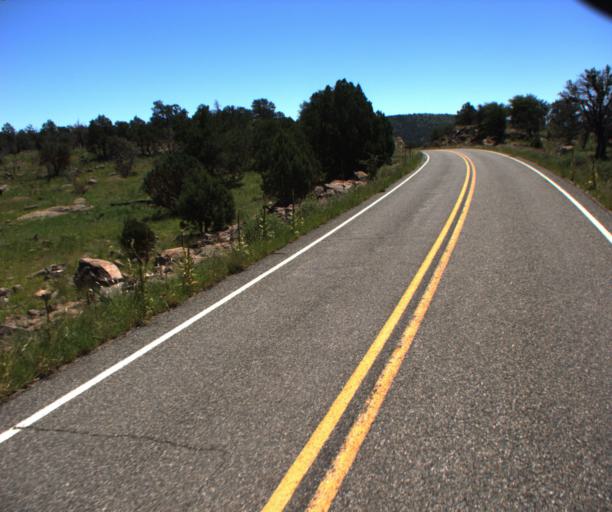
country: US
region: Arizona
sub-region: Greenlee County
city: Morenci
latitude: 33.2947
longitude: -109.3605
